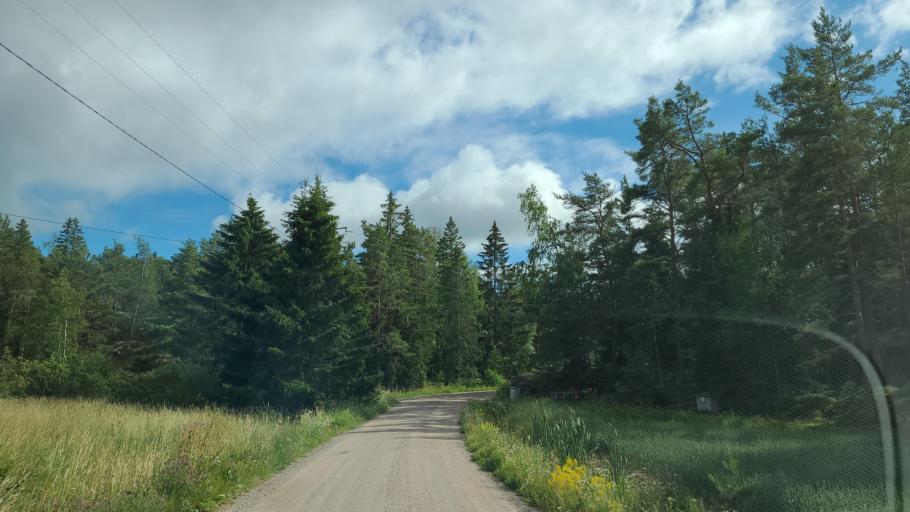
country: FI
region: Varsinais-Suomi
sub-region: Aboland-Turunmaa
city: Nagu
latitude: 60.1975
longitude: 21.7759
